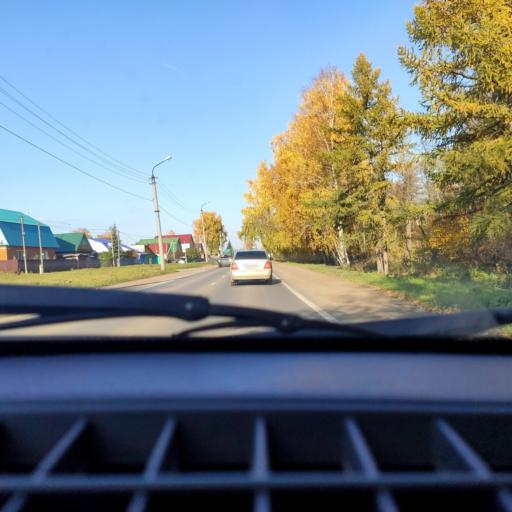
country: RU
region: Bashkortostan
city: Ufa
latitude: 54.8122
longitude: 56.1619
